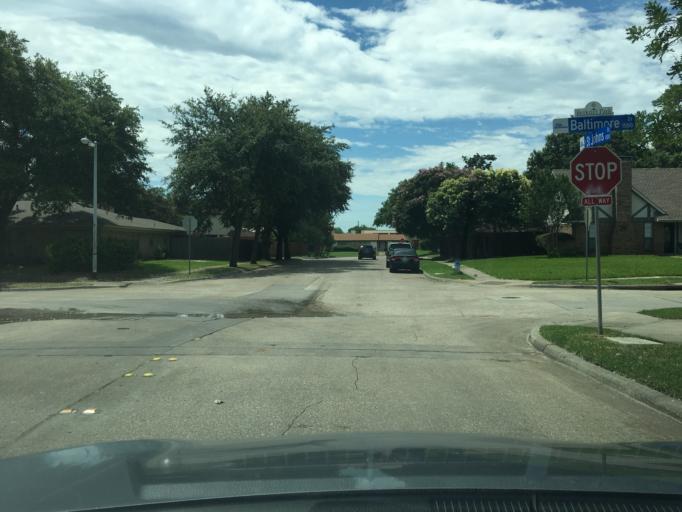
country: US
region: Texas
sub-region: Dallas County
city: Richardson
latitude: 32.9338
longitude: -96.6952
